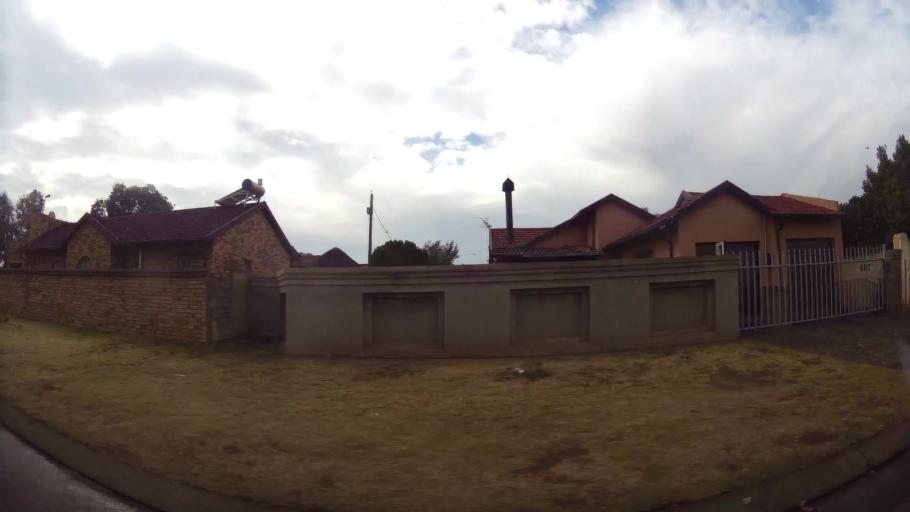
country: ZA
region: Gauteng
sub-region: Ekurhuleni Metropolitan Municipality
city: Germiston
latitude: -26.3295
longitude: 28.1908
